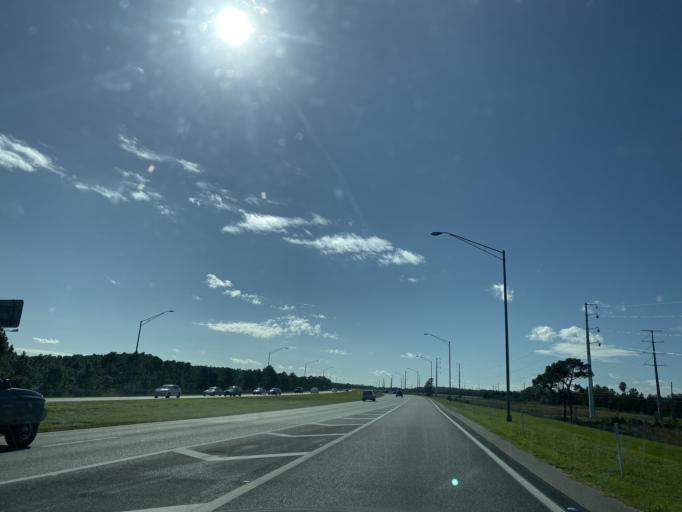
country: US
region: Florida
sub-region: Orange County
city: Meadow Woods
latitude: 28.3981
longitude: -81.2492
